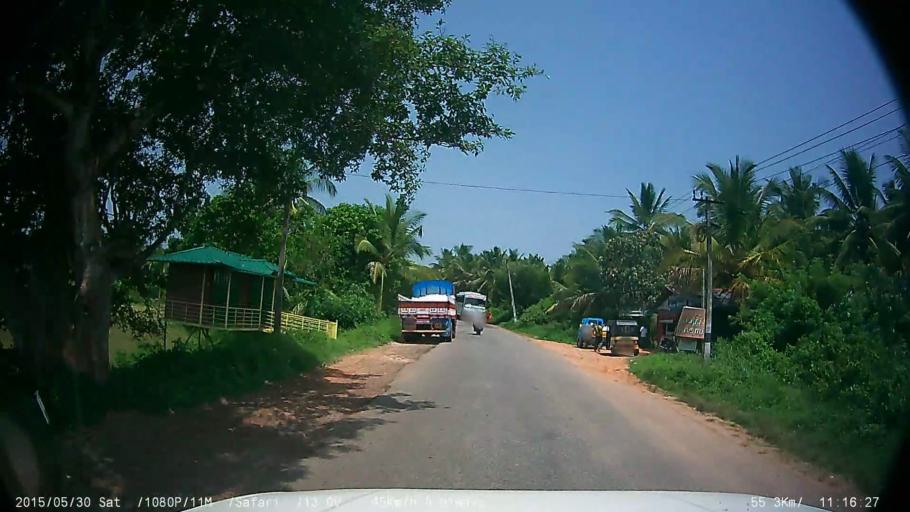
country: IN
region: Kerala
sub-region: Wayanad
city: Panamaram
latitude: 11.7762
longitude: 76.0563
